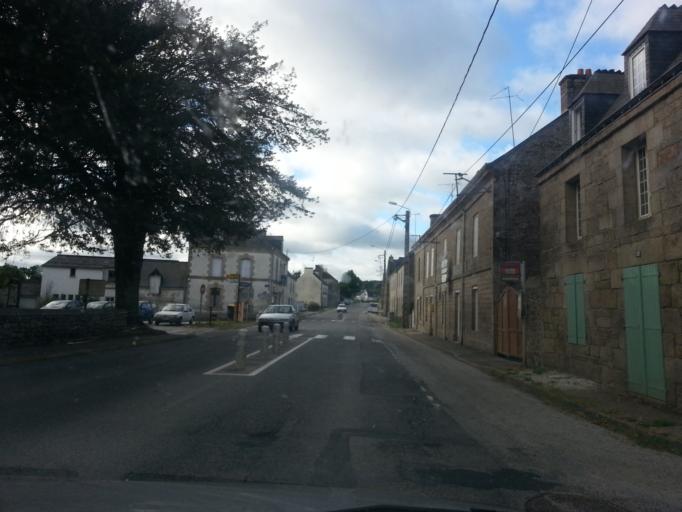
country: FR
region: Brittany
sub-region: Departement du Morbihan
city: Pontivy
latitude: 48.0850
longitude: -2.9936
